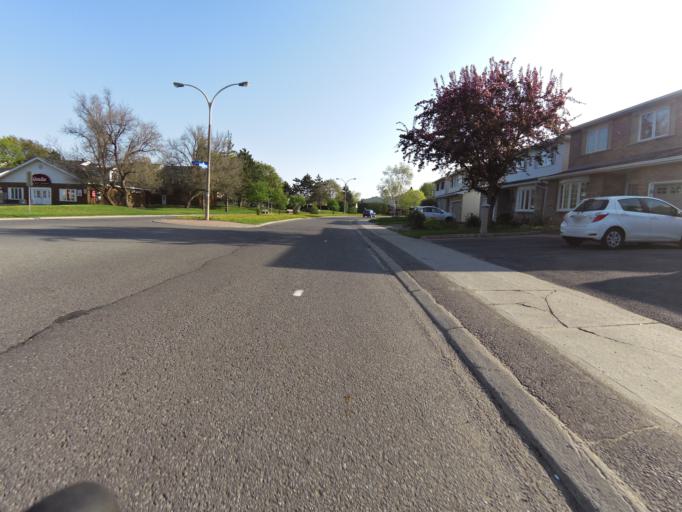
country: CA
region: Ontario
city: Bells Corners
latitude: 45.3330
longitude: -75.7708
